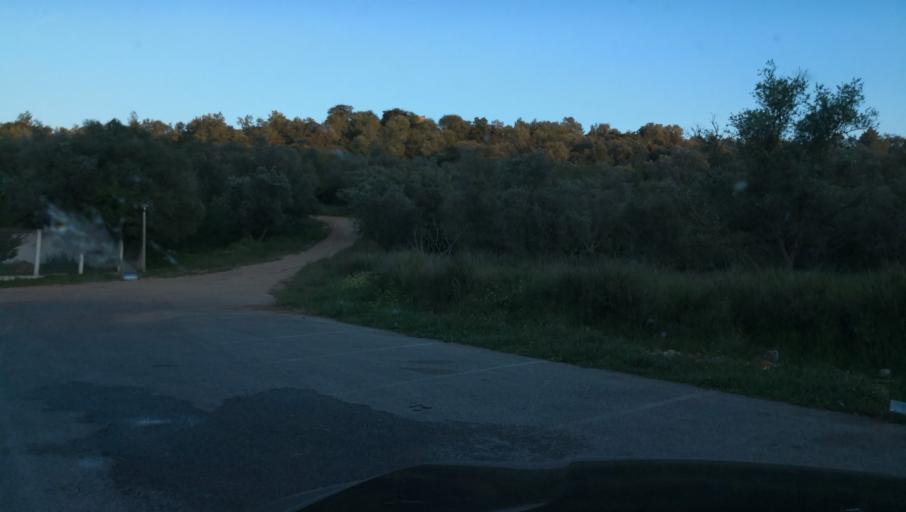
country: PT
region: Setubal
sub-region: Setubal
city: Setubal
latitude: 38.5225
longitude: -8.9158
